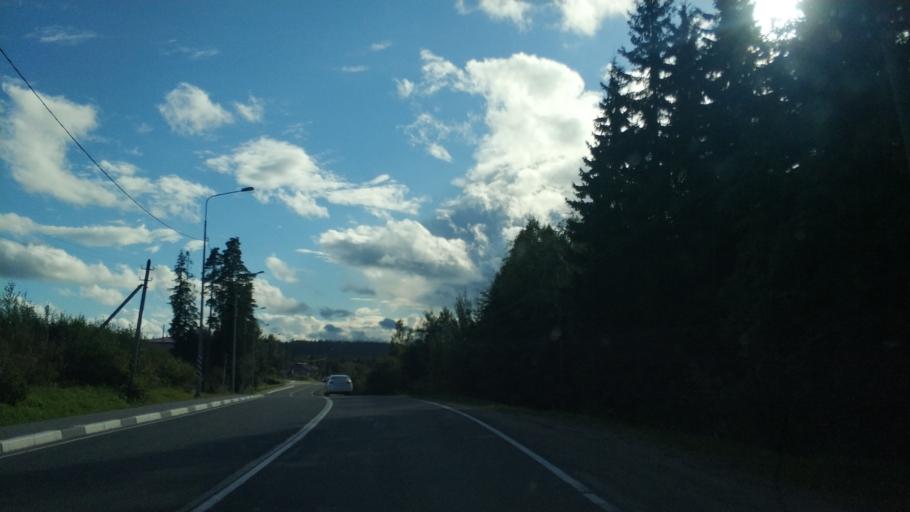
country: RU
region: Republic of Karelia
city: Lakhdenpokh'ya
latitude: 61.5213
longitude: 30.1583
